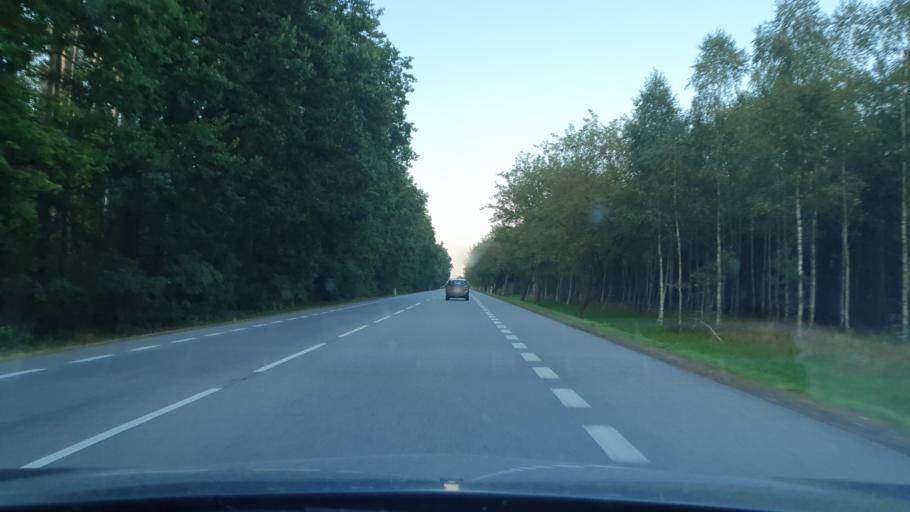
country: PL
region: Pomeranian Voivodeship
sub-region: Powiat leborski
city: Nowa Wies Leborska
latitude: 54.4954
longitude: 17.6165
